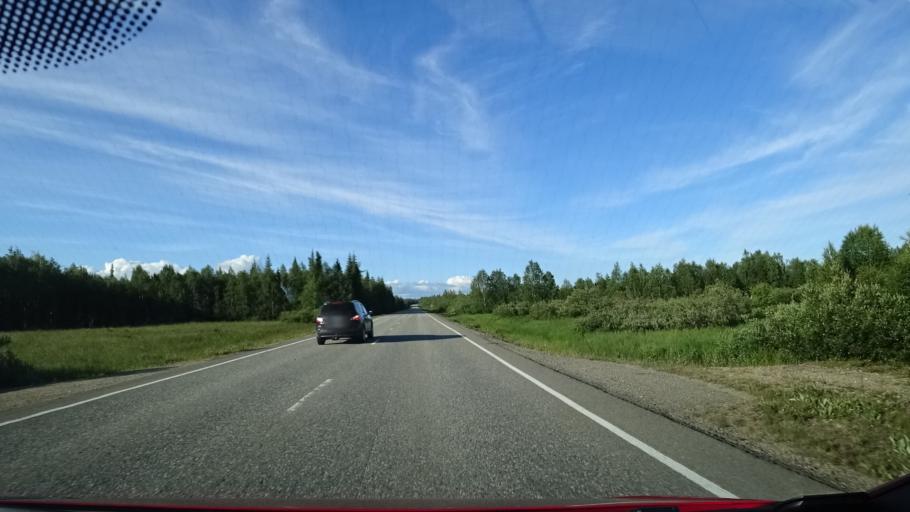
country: FI
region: Lapland
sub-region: Pohjois-Lappi
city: Sodankylae
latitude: 67.9563
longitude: 26.7839
